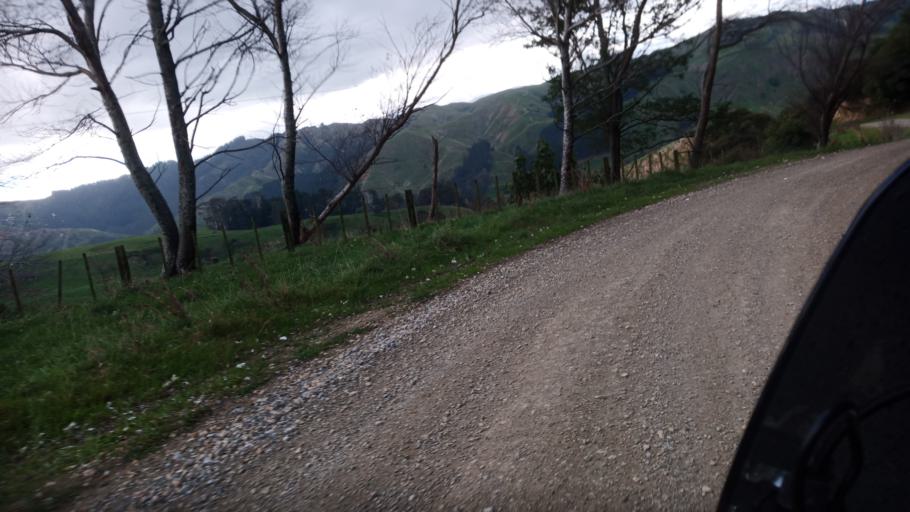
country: NZ
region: Gisborne
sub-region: Gisborne District
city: Gisborne
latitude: -38.4628
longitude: 177.6299
